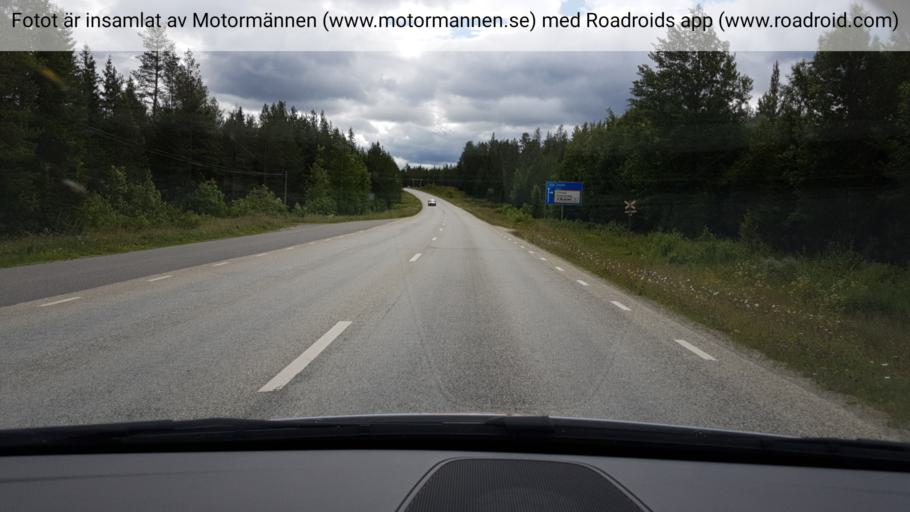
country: SE
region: Jaemtland
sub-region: Bergs Kommun
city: Hoverberg
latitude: 62.5099
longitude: 14.1952
